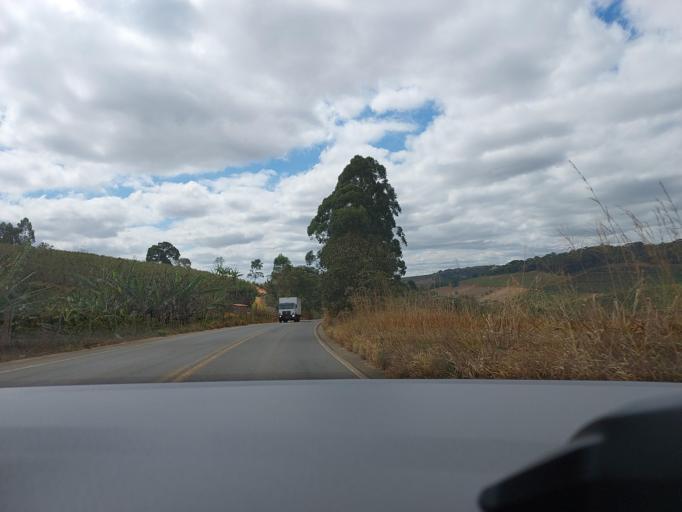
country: BR
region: Minas Gerais
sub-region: Vicosa
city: Vicosa
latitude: -20.8397
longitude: -42.7034
